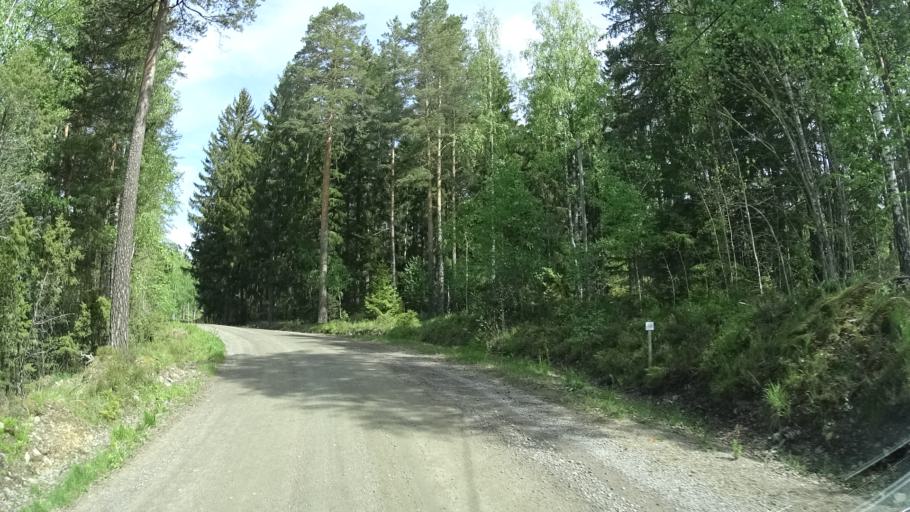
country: SE
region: OEstergoetland
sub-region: Finspangs Kommun
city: Finspang
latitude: 58.7566
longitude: 15.8359
